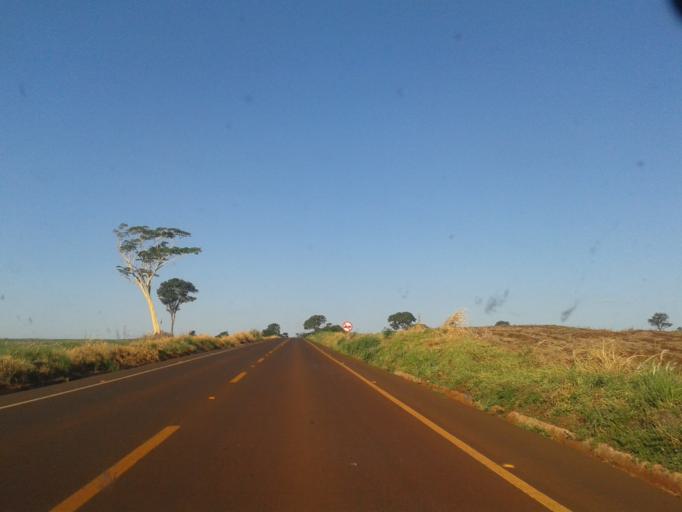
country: BR
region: Minas Gerais
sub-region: Capinopolis
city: Capinopolis
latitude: -18.7121
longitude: -49.7975
